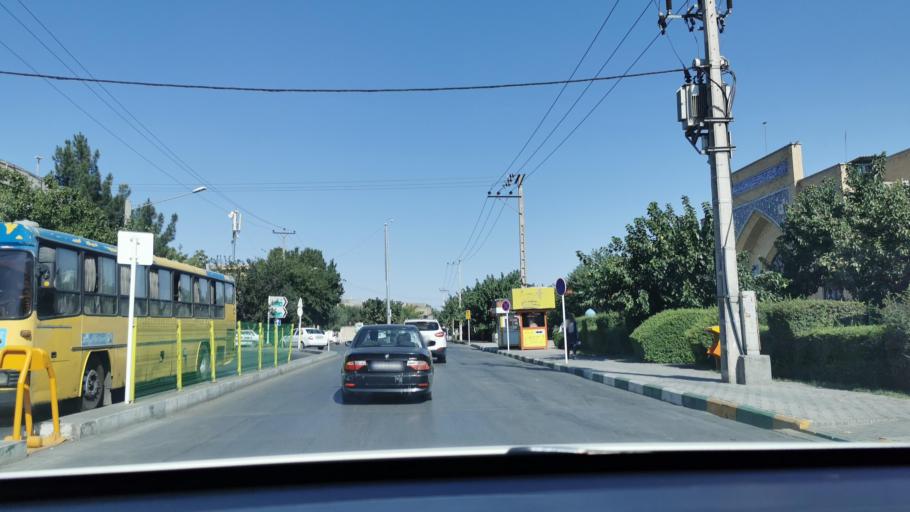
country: IR
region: Razavi Khorasan
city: Mashhad
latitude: 36.3407
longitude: 59.6289
